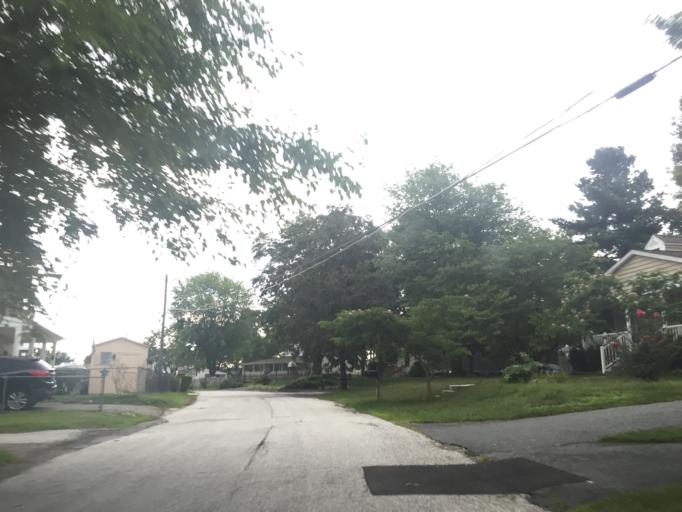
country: US
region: Maryland
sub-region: Baltimore County
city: Carney
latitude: 39.3960
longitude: -76.5302
